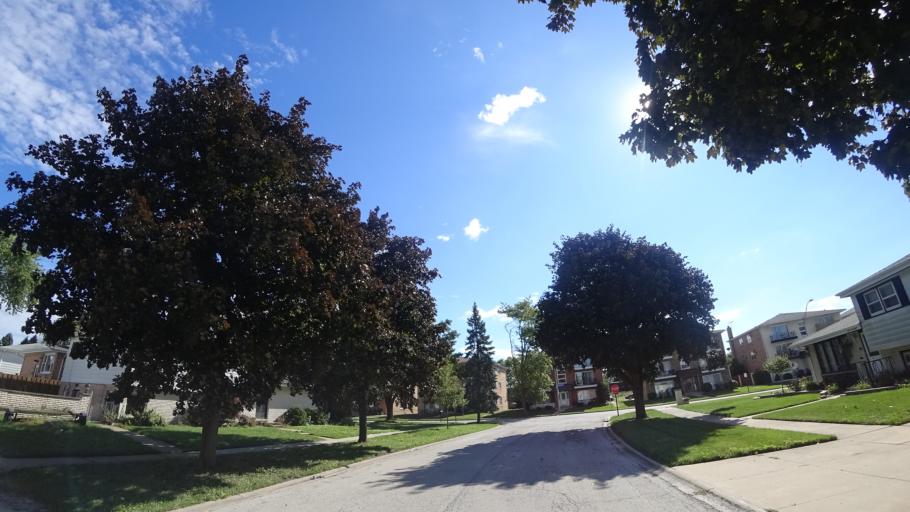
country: US
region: Illinois
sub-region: Cook County
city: Chicago Ridge
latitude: 41.7034
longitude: -87.7708
